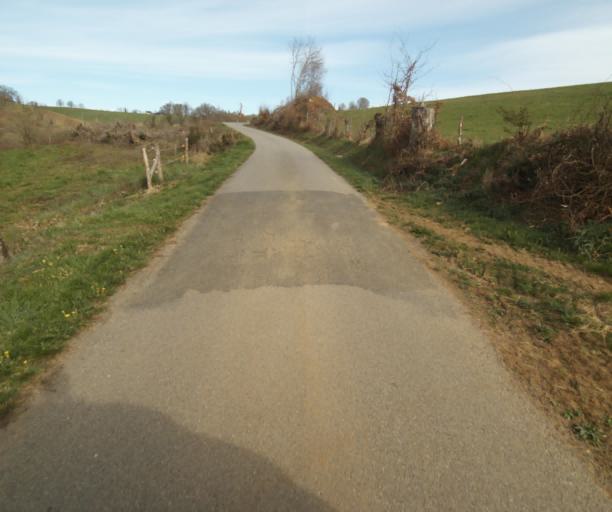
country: FR
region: Limousin
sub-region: Departement de la Correze
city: Chamboulive
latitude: 45.4167
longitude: 1.7907
